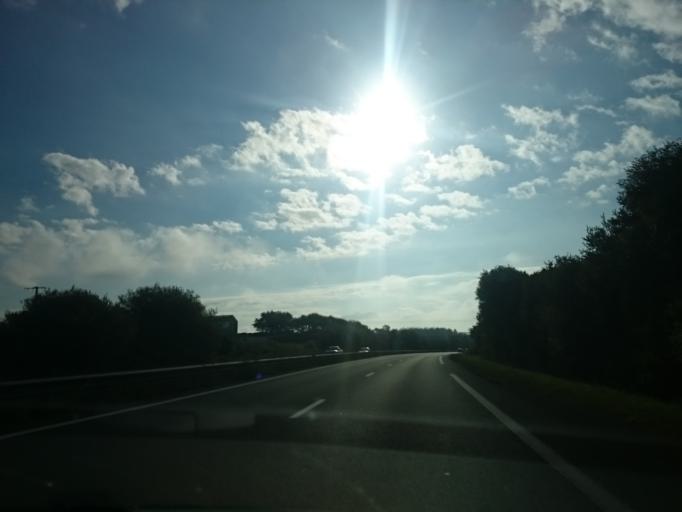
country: FR
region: Brittany
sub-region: Departement du Finistere
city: Guerlesquin
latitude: 48.5639
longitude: -3.5291
